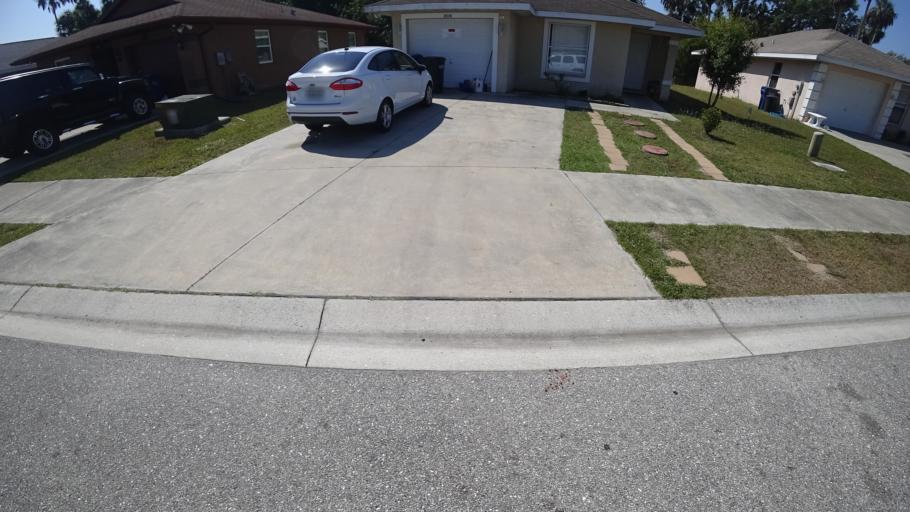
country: US
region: Florida
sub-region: Manatee County
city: Samoset
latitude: 27.4726
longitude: -82.5288
